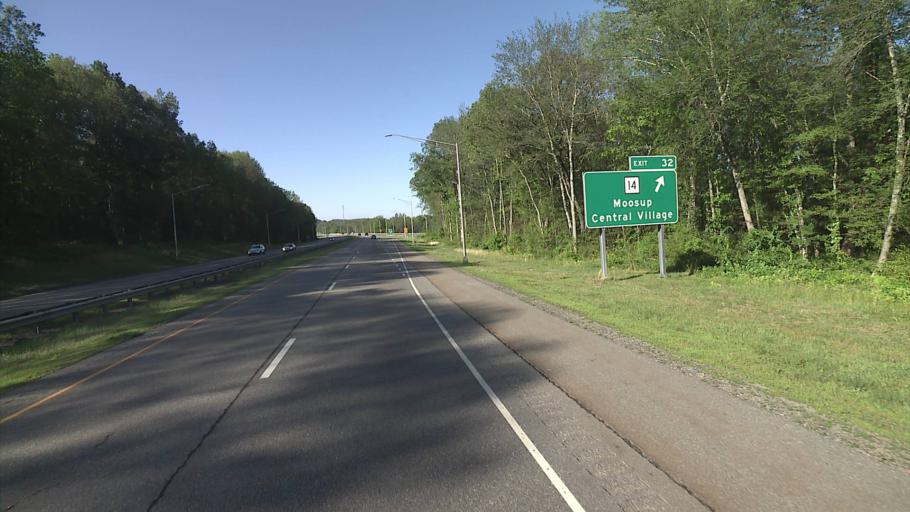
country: US
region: Connecticut
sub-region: Windham County
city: Moosup
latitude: 41.7235
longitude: -71.8925
